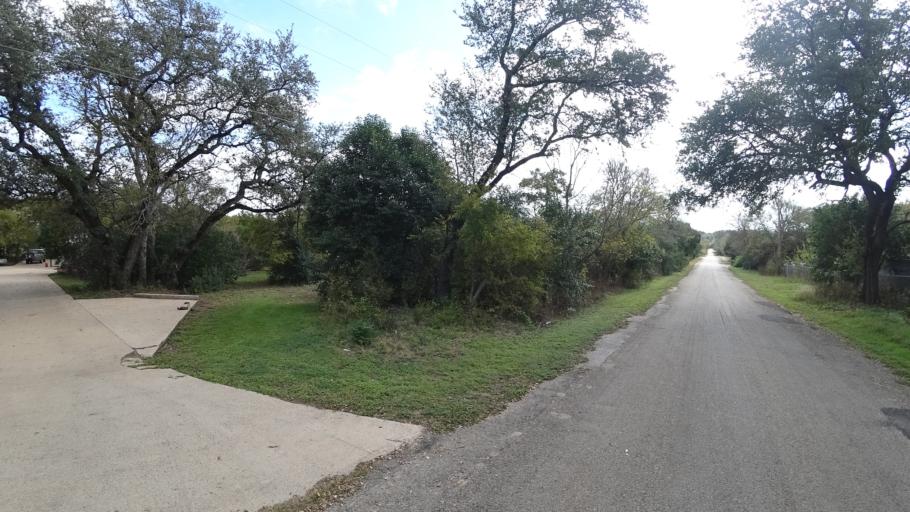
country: US
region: Texas
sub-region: Travis County
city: Barton Creek
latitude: 30.2485
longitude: -97.9218
